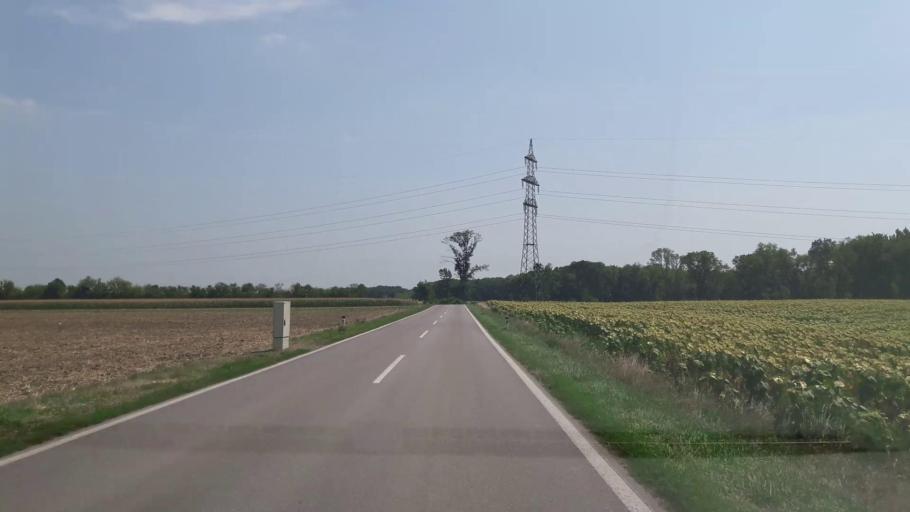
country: AT
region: Lower Austria
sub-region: Politischer Bezirk Bruck an der Leitha
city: Gotzendorf an der Leitha
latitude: 48.0203
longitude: 16.6016
